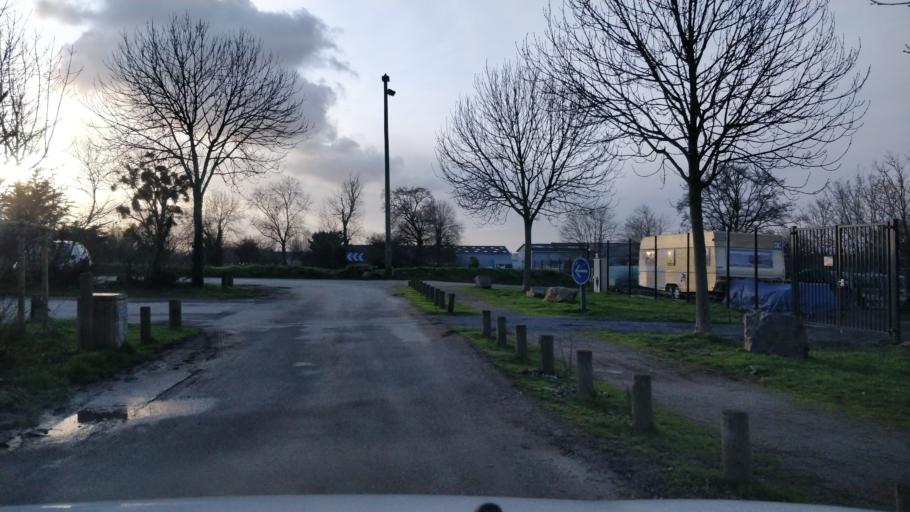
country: FR
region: Brittany
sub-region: Departement d'Ille-et-Vilaine
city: Saint-Jacques-de-la-Lande
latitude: 48.1028
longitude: -1.7202
